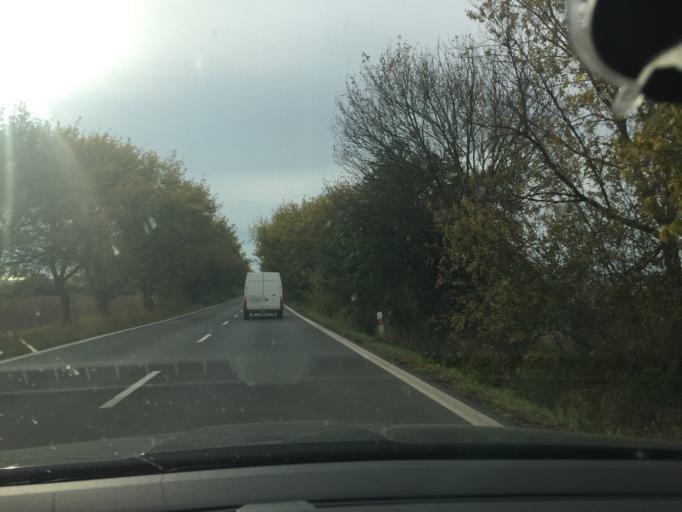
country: CZ
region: Central Bohemia
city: Zelenec
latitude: 50.1195
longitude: 14.6517
